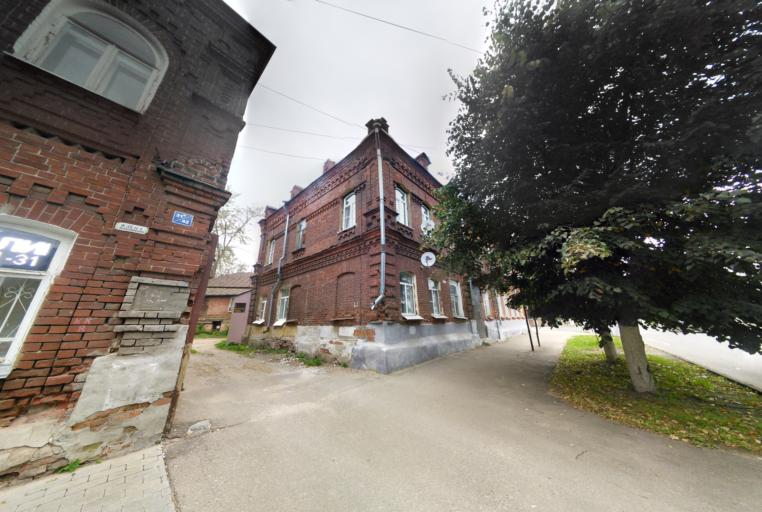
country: RU
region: Kostroma
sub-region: Kostromskoy Rayon
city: Kostroma
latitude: 57.7722
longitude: 40.9301
